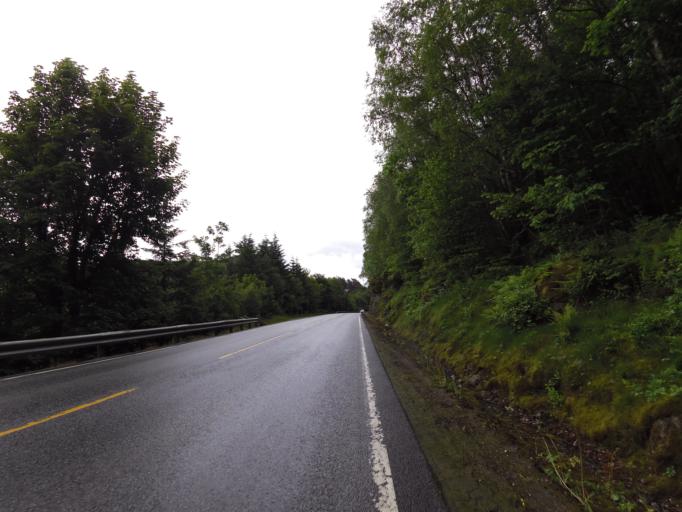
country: NO
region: Vest-Agder
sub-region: Farsund
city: Farsund
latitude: 58.1023
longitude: 6.8519
